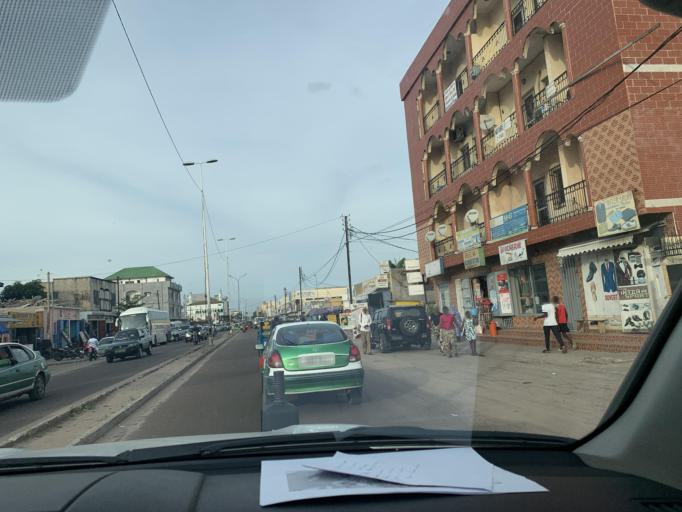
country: CG
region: Brazzaville
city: Brazzaville
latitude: -4.2532
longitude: 15.2749
